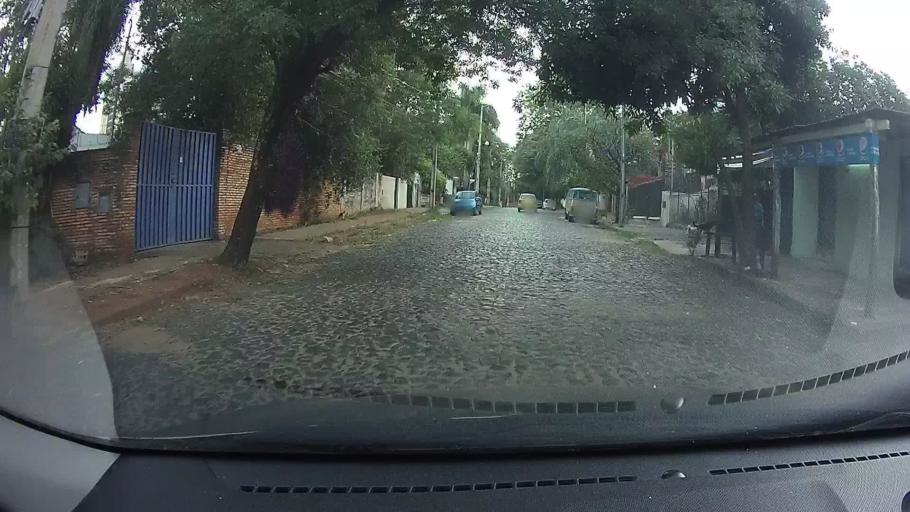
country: PY
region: Asuncion
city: Asuncion
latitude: -25.2672
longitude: -57.5702
